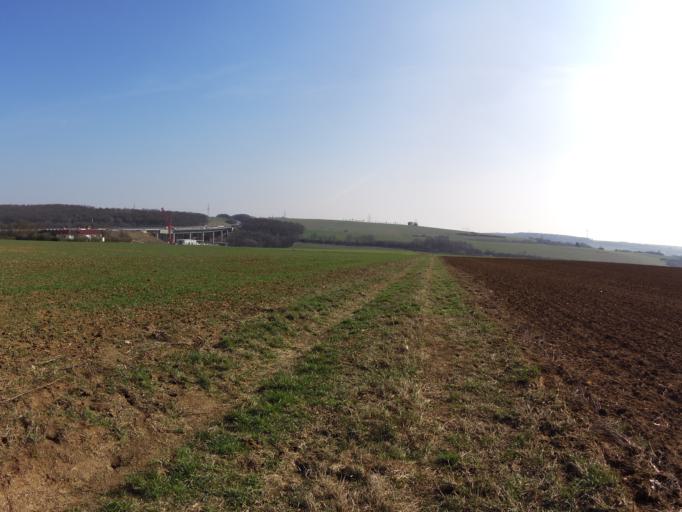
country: DE
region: Bavaria
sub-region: Regierungsbezirk Unterfranken
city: Rottendorf
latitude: 49.8081
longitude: 10.0402
